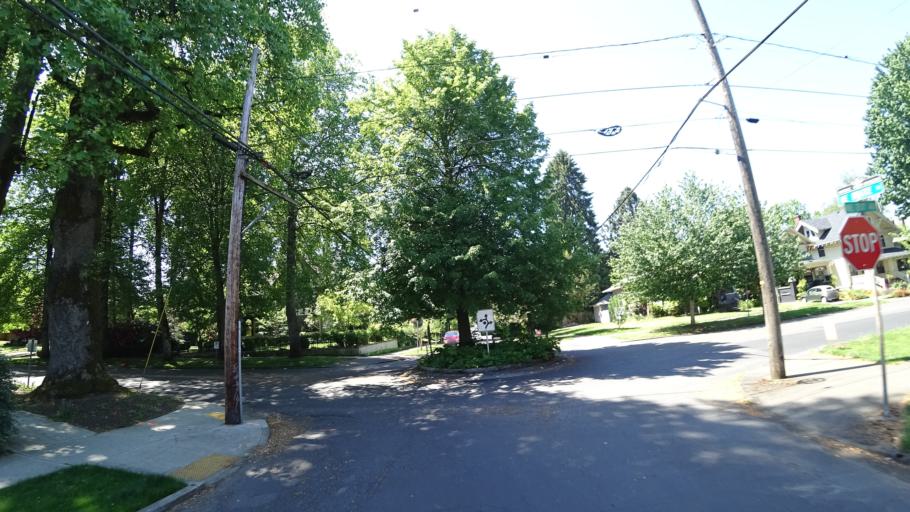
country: US
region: Oregon
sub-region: Multnomah County
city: Portland
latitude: 45.5405
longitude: -122.6441
